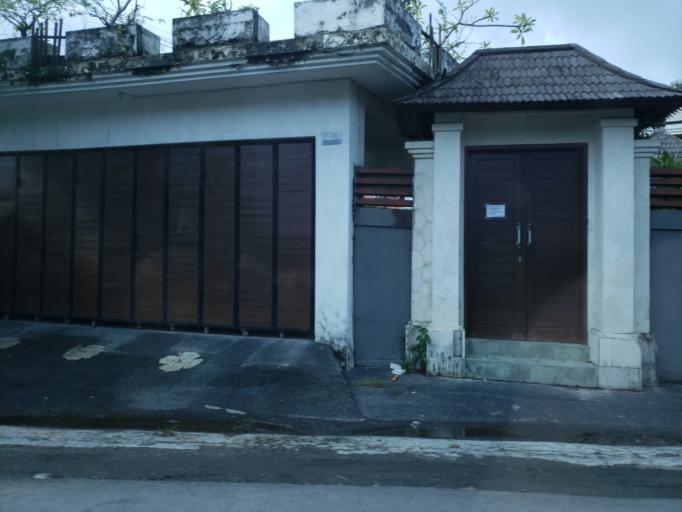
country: ID
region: Bali
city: Kuta
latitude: -8.6826
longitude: 115.1692
